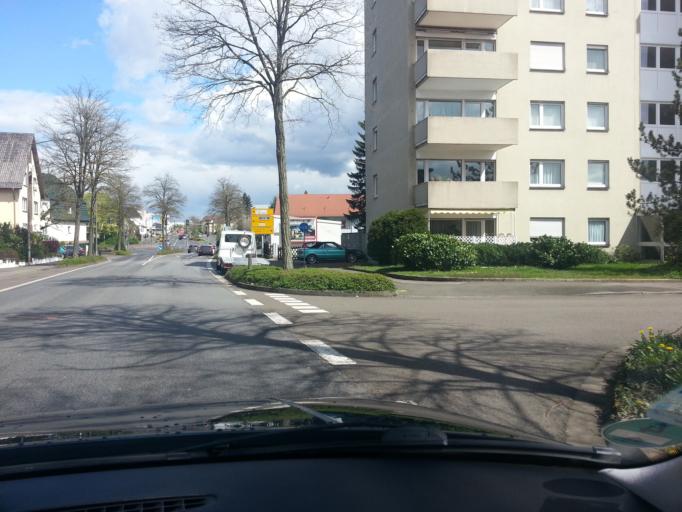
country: DE
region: Saarland
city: Homburg
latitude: 49.3215
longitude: 7.3303
